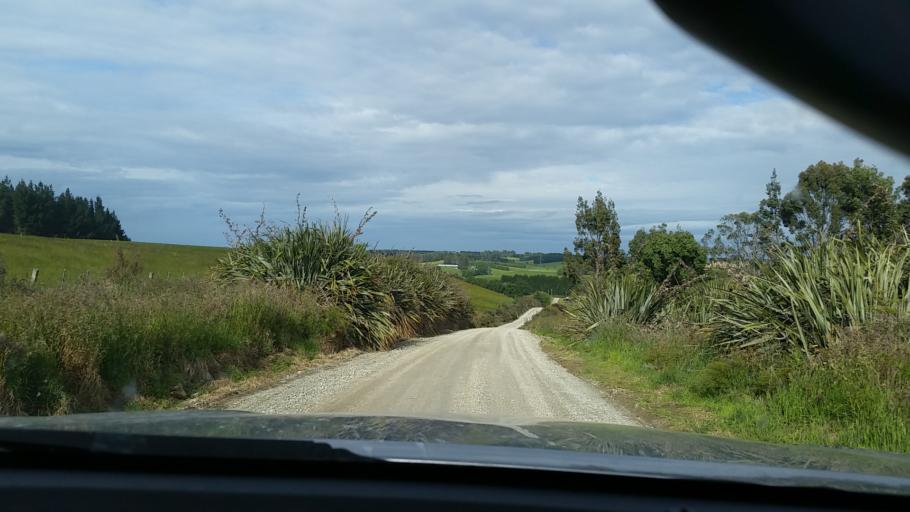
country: NZ
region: Southland
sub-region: Gore District
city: Gore
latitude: -46.2051
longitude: 168.7821
